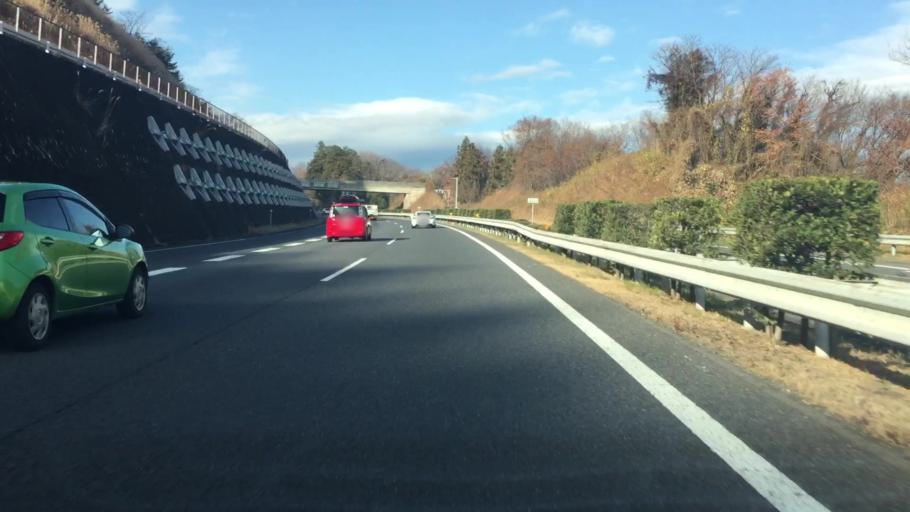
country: JP
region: Gunma
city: Tomioka
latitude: 36.2376
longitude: 138.8591
